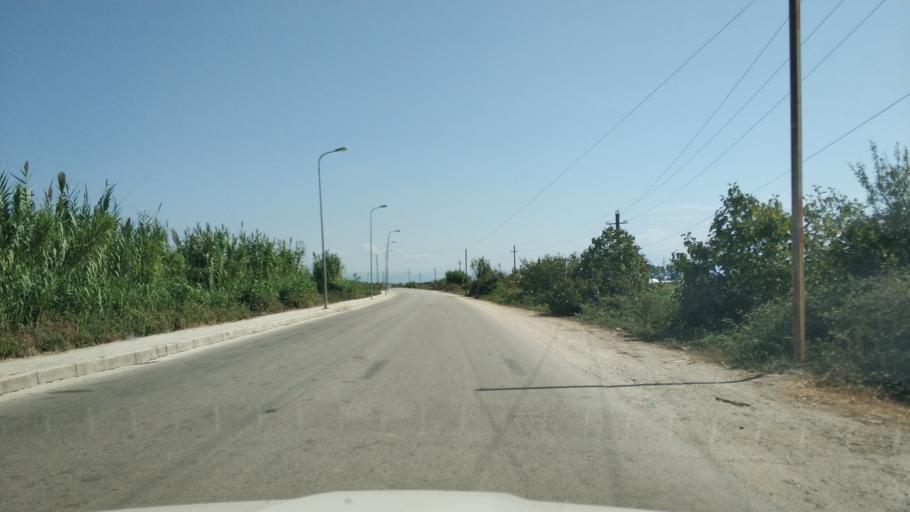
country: AL
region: Fier
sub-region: Rrethi i Lushnjes
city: Gradishte
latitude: 40.8838
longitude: 19.5816
